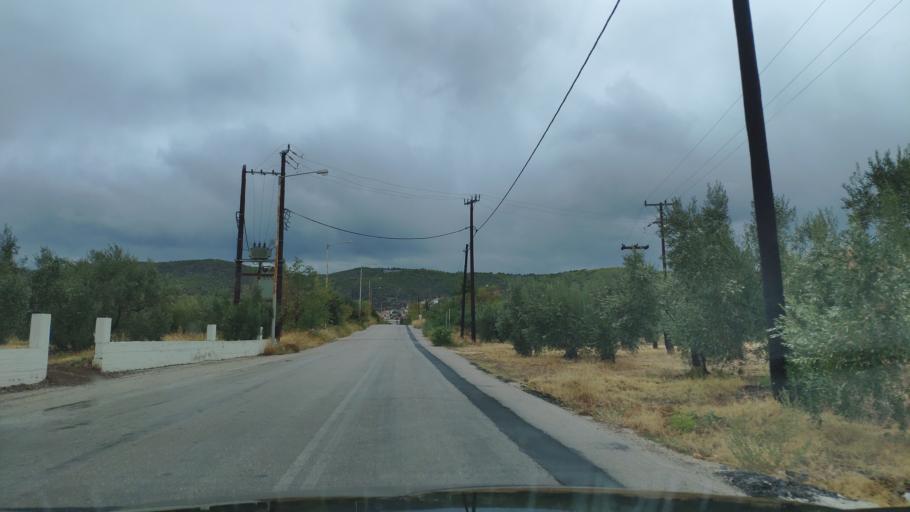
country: GR
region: Peloponnese
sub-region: Nomos Korinthias
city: Perachora
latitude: 38.0191
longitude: 22.9474
